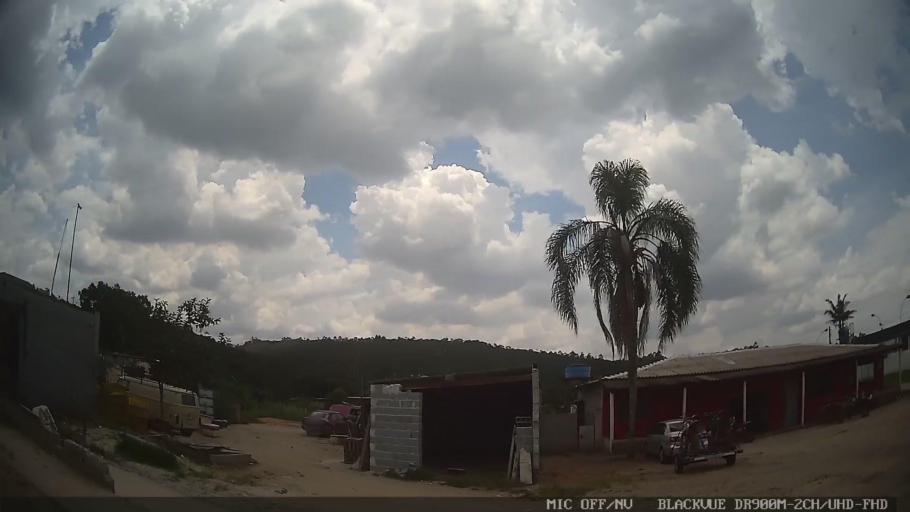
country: BR
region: Sao Paulo
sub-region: Ferraz De Vasconcelos
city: Ferraz de Vasconcelos
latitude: -23.6142
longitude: -46.3772
